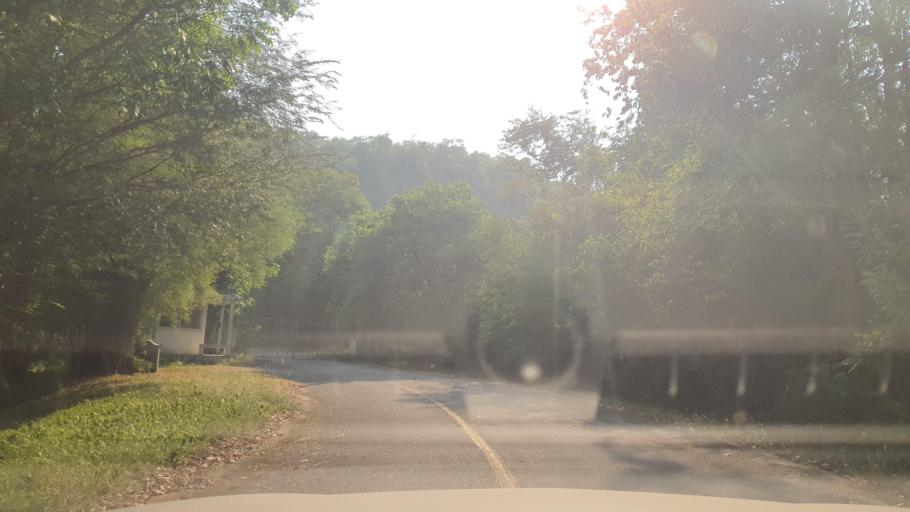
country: TH
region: Kanchanaburi
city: Sai Yok
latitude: 14.2254
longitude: 99.2243
